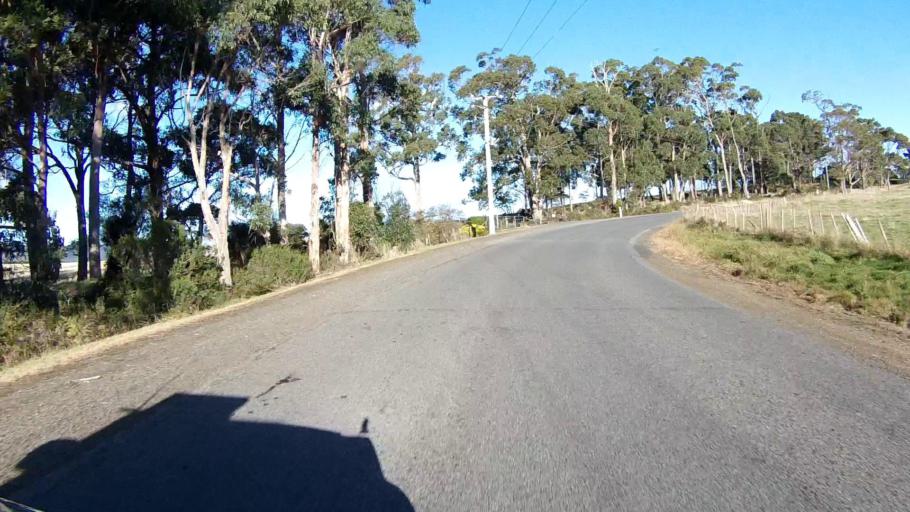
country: AU
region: Tasmania
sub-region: Clarence
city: Sandford
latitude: -43.1665
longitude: 147.8599
